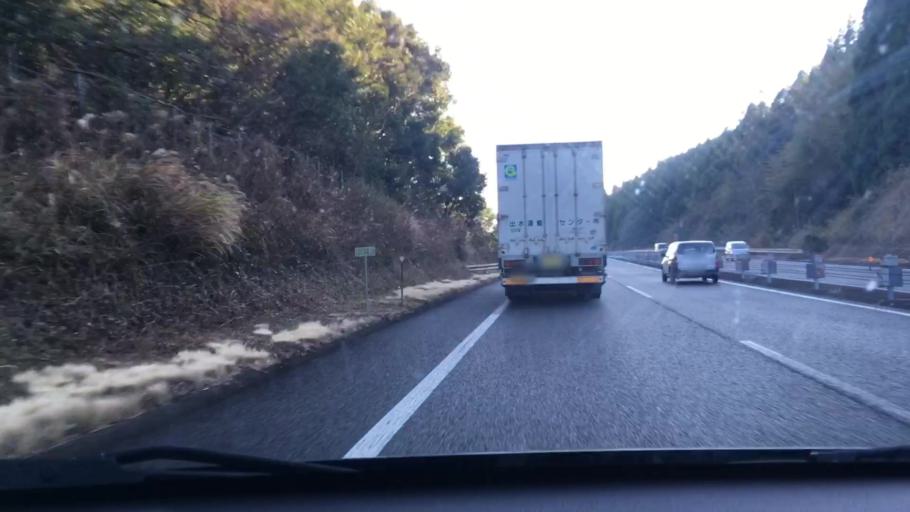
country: JP
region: Kagoshima
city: Kajiki
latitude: 31.8274
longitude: 130.6939
